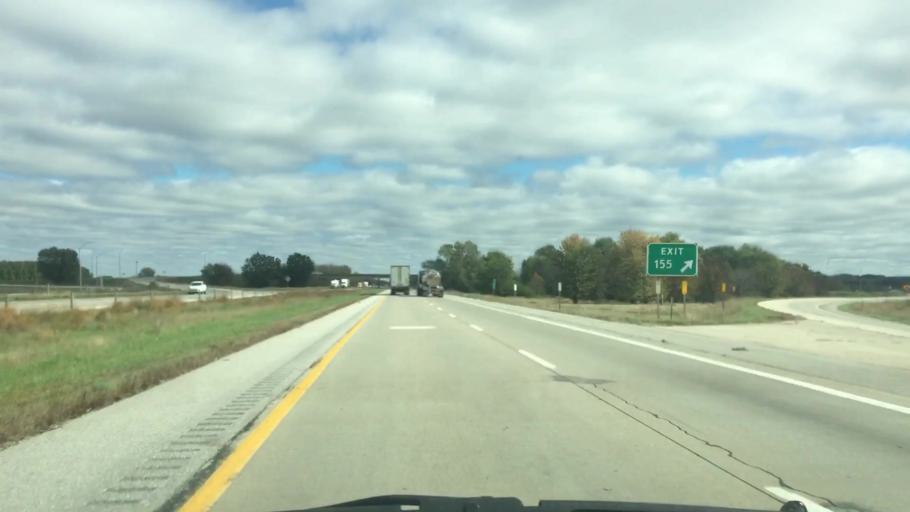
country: US
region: Iowa
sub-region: Jasper County
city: Colfax
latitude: 41.6909
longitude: -93.2522
